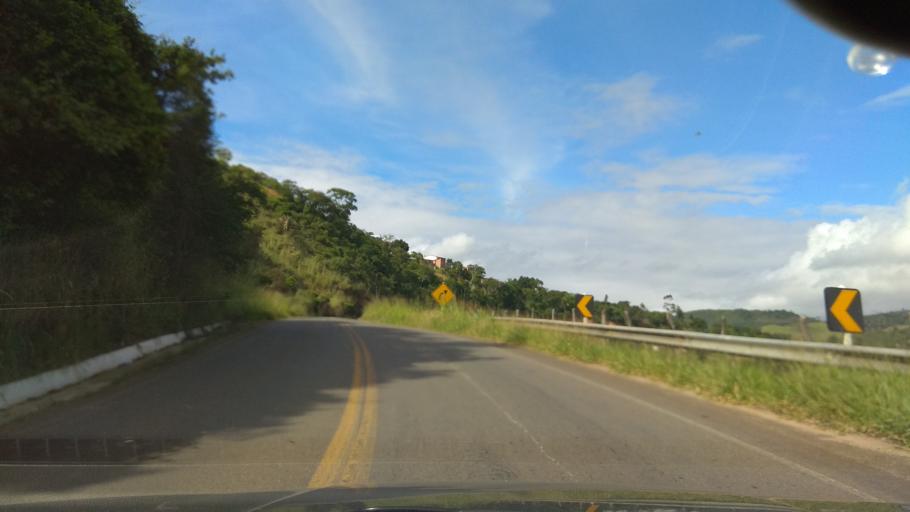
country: BR
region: Bahia
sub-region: Ubaira
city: Ubaira
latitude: -13.2552
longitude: -39.6640
